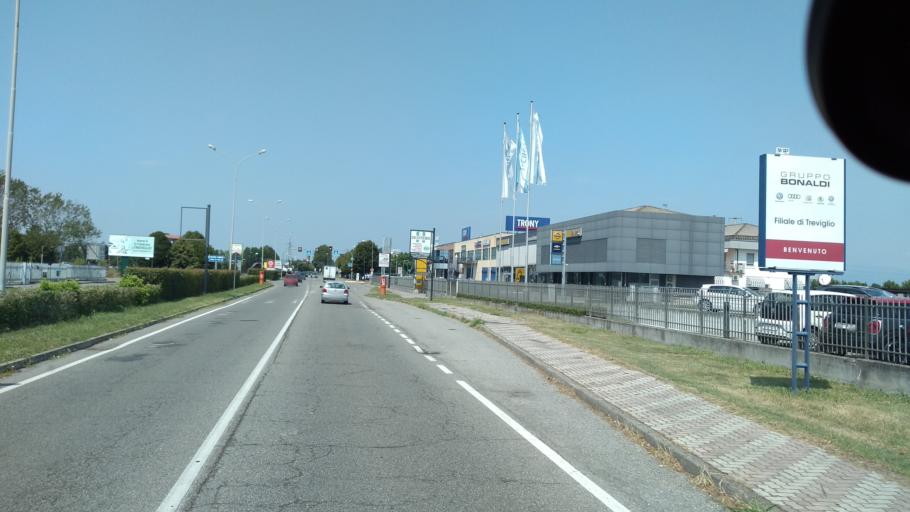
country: IT
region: Lombardy
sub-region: Provincia di Bergamo
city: Calvenzano
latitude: 45.5100
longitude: 9.6155
